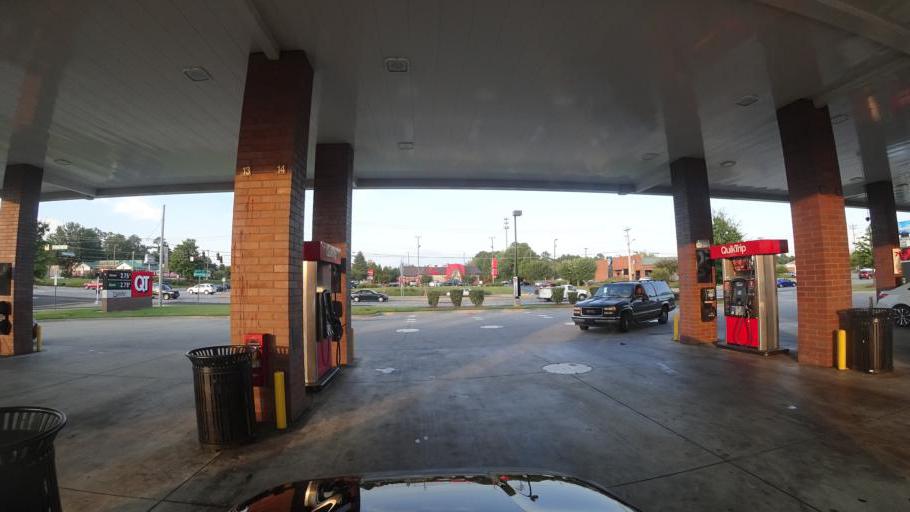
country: US
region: Georgia
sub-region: Gwinnett County
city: Lilburn
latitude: 33.9432
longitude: -84.1244
